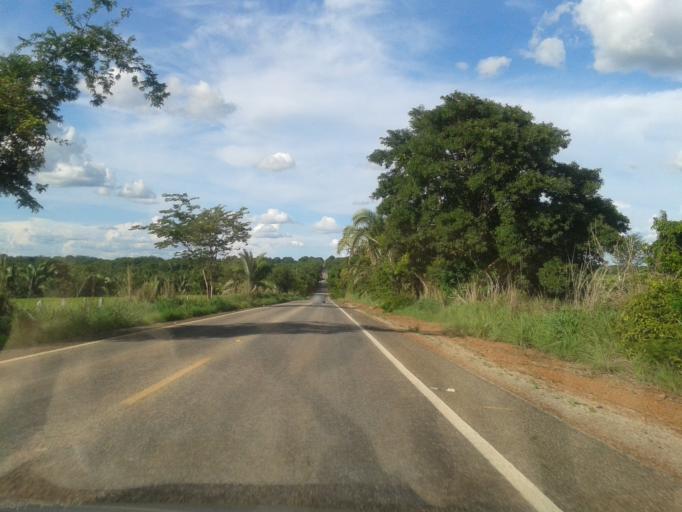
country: BR
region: Goias
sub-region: Mozarlandia
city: Mozarlandia
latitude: -14.4604
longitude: -50.4661
